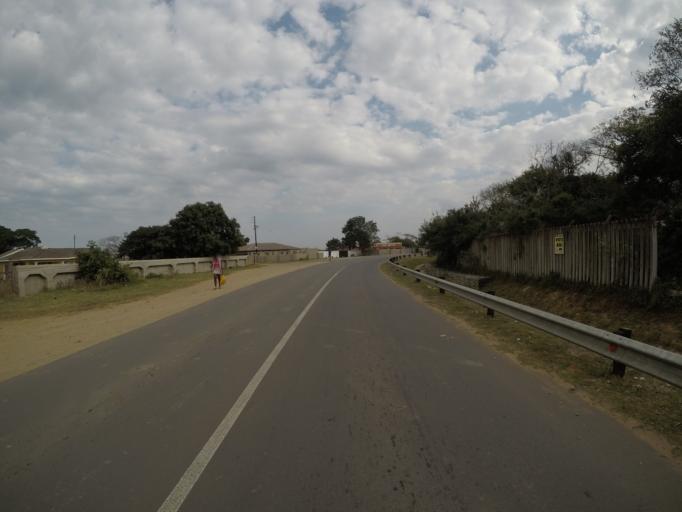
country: ZA
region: KwaZulu-Natal
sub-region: uThungulu District Municipality
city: Richards Bay
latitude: -28.7485
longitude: 32.0870
